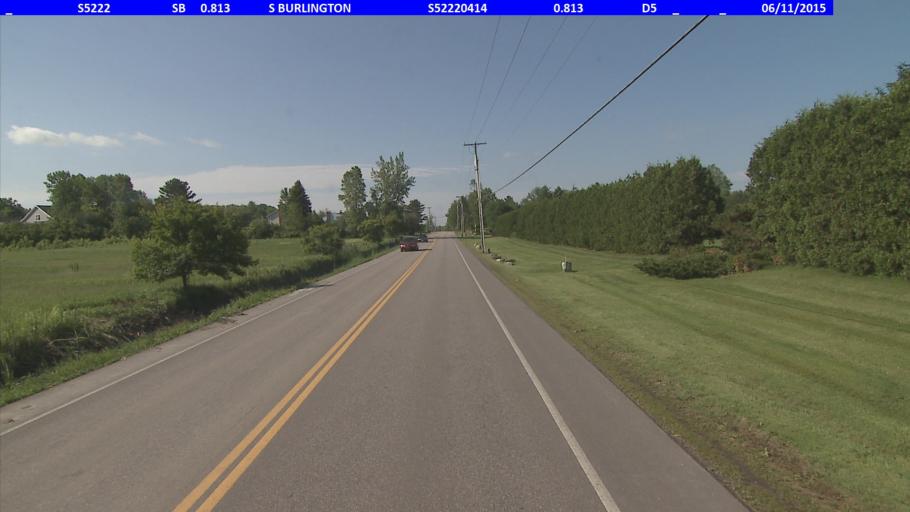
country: US
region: Vermont
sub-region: Chittenden County
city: South Burlington
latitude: 44.4283
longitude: -73.1939
